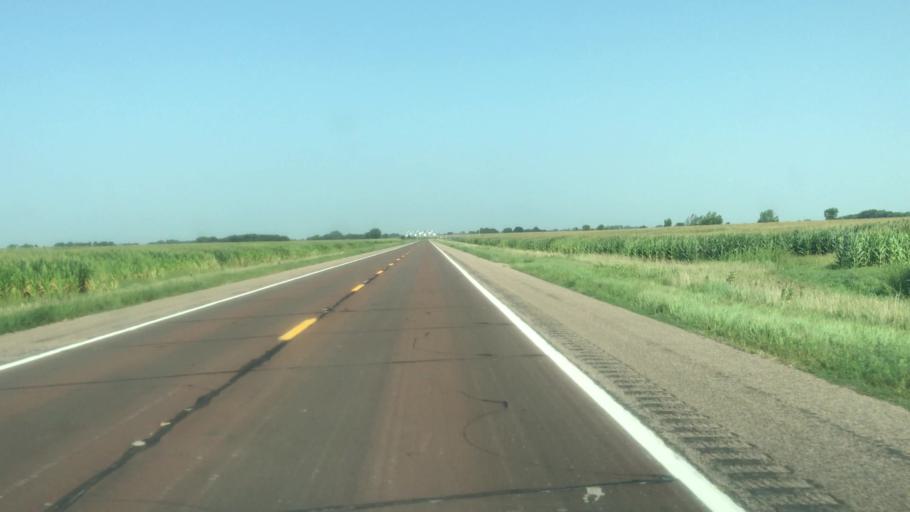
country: US
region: Nebraska
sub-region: Hall County
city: Wood River
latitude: 40.9806
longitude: -98.5218
